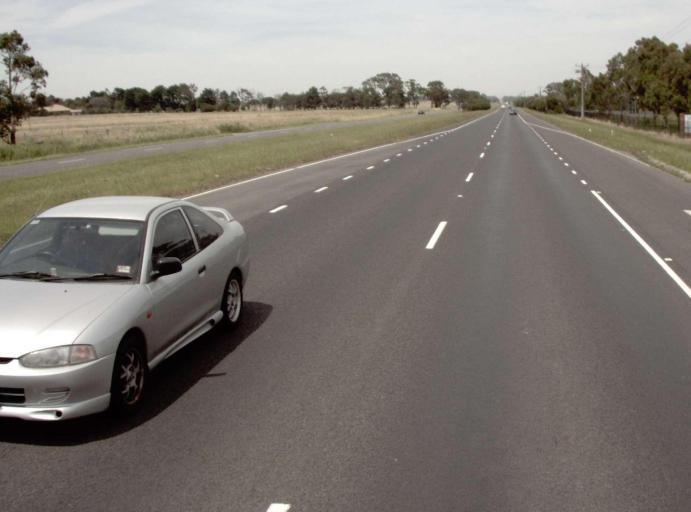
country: AU
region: Victoria
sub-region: Frankston
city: Skye
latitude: -38.0929
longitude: 145.2364
